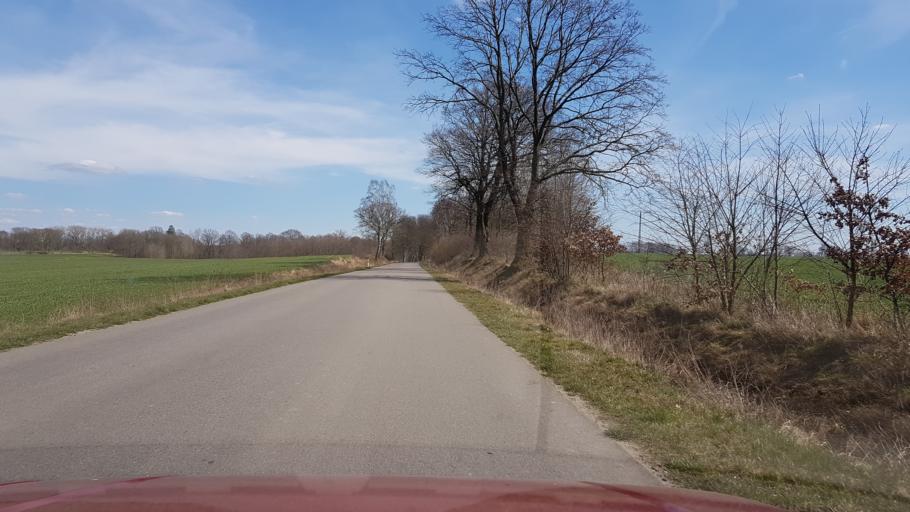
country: PL
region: West Pomeranian Voivodeship
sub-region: Powiat koszalinski
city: Mielno
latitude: 54.1574
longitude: 16.0646
